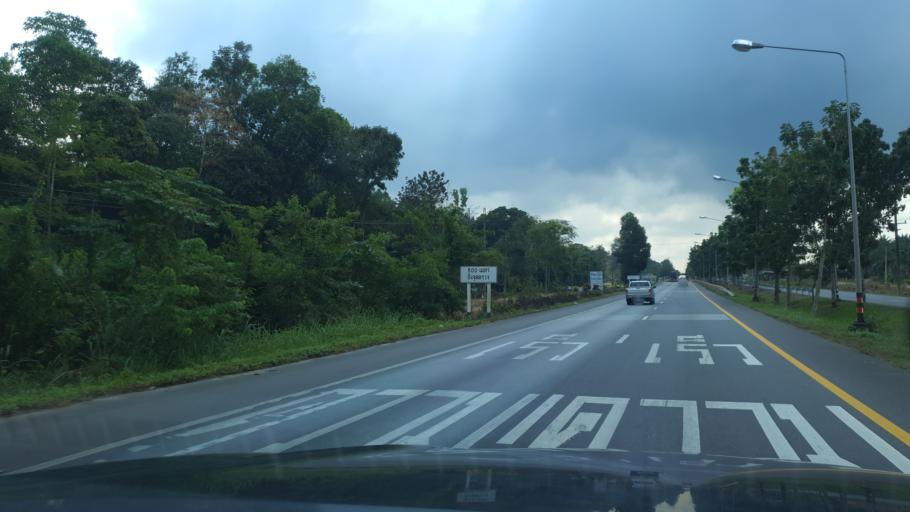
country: TH
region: Chumphon
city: Tha Sae
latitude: 10.7558
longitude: 99.2017
